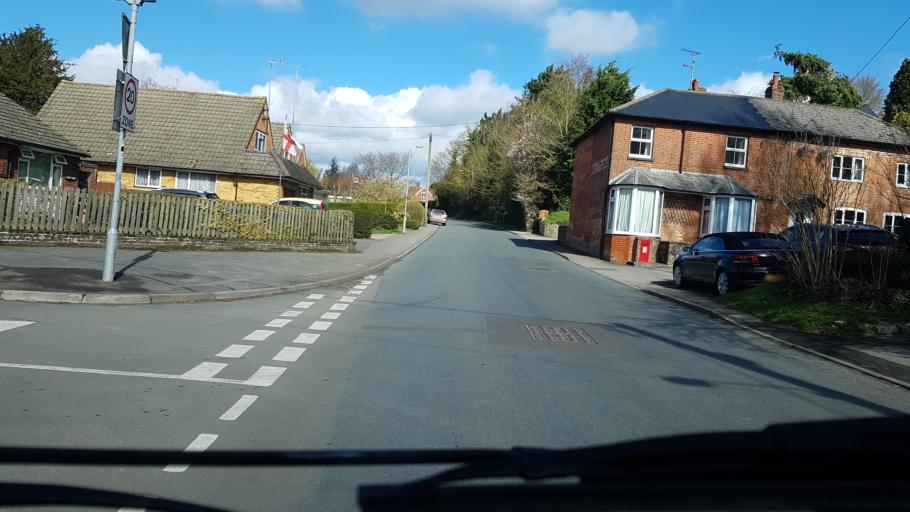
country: GB
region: England
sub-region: Wiltshire
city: Market Lavington
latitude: 51.2957
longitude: -1.9711
